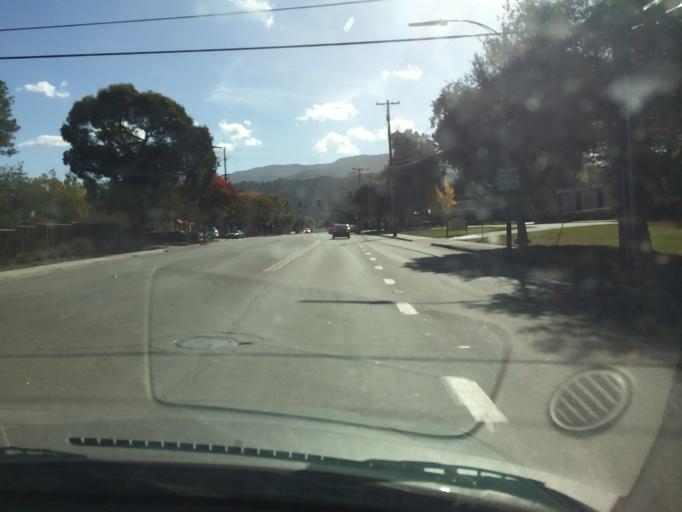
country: US
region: California
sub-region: Santa Clara County
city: Cambrian Park
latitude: 37.2449
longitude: -121.9313
